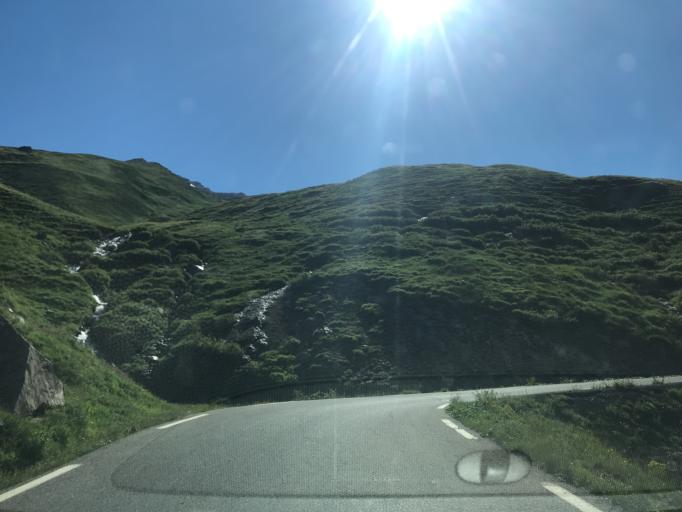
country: IT
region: Piedmont
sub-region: Provincia di Cuneo
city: Pontechianale
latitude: 44.6993
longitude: 6.9454
